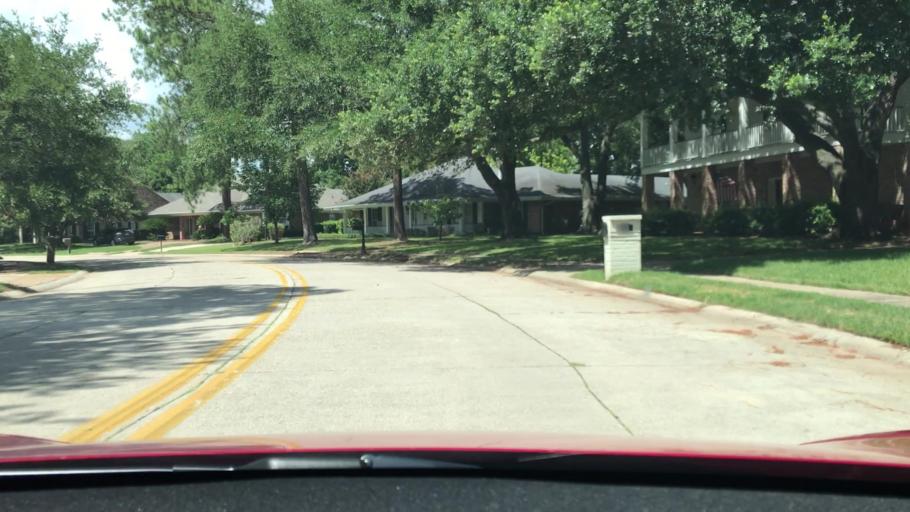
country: US
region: Louisiana
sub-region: Bossier Parish
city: Bossier City
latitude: 32.4260
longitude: -93.7277
